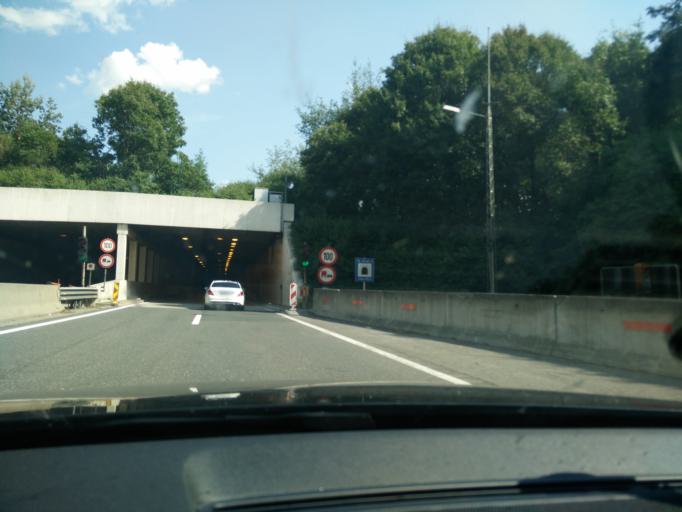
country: AT
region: Carinthia
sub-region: Villach Stadt
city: Villach
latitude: 46.6418
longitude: 13.8868
